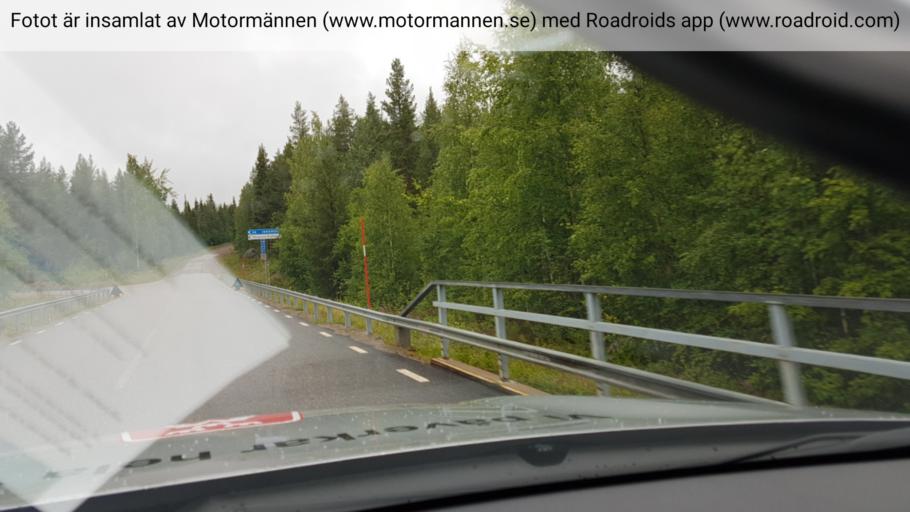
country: SE
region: Norrbotten
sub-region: Gallivare Kommun
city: Gaellivare
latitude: 66.6866
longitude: 20.3640
